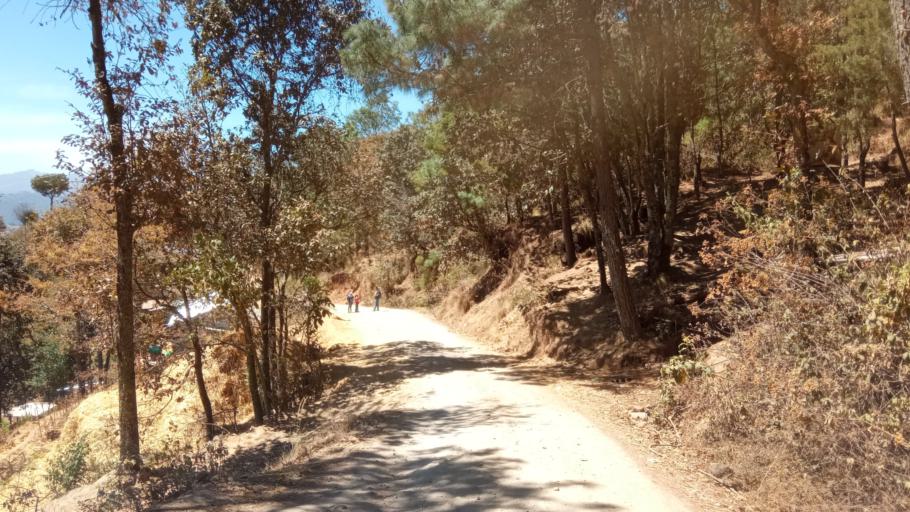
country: GT
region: San Marcos
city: Tejutla
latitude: 15.1369
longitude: -91.7932
